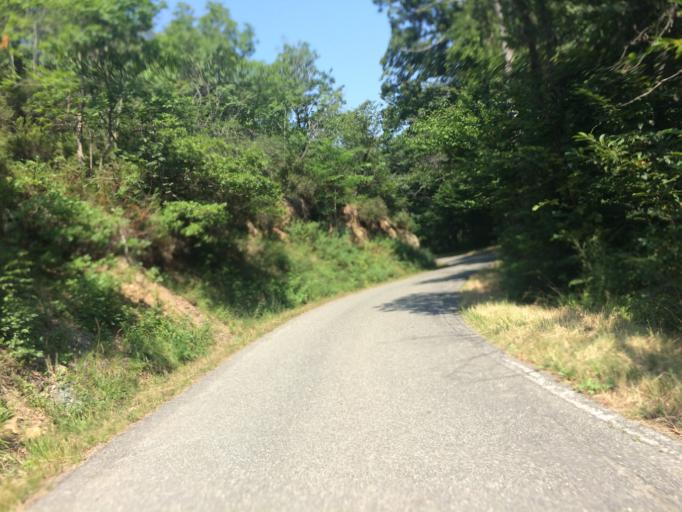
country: IT
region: Piedmont
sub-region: Provincia di Alessandria
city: Malvicino
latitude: 44.5387
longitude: 8.4106
